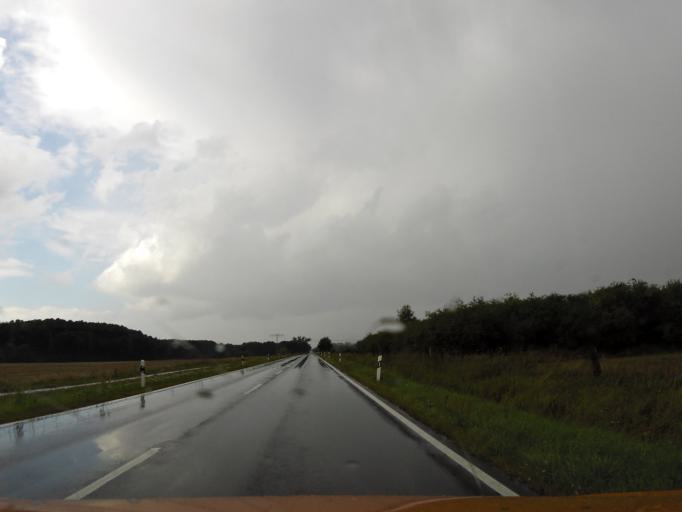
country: DE
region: Brandenburg
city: Wustermark
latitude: 52.4789
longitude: 12.9449
